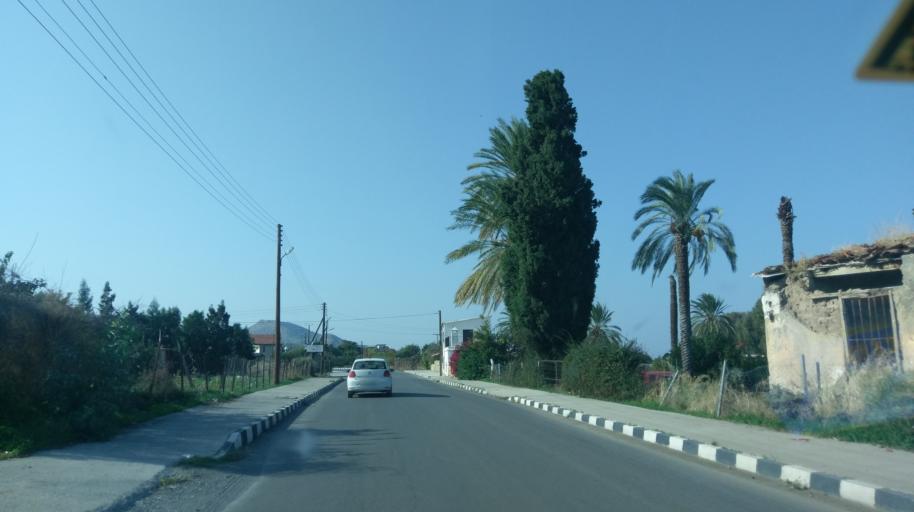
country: CY
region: Lefkosia
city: Lefka
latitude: 35.1419
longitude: 32.8145
